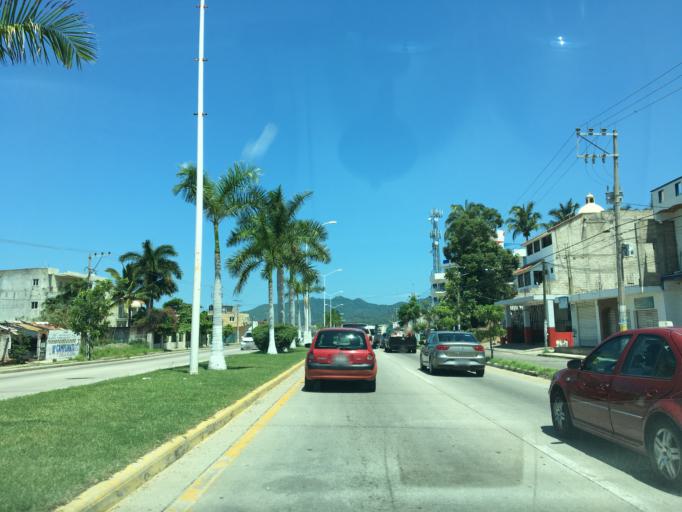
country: MX
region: Nayarit
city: Bucerias
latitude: 20.7540
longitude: -105.3328
